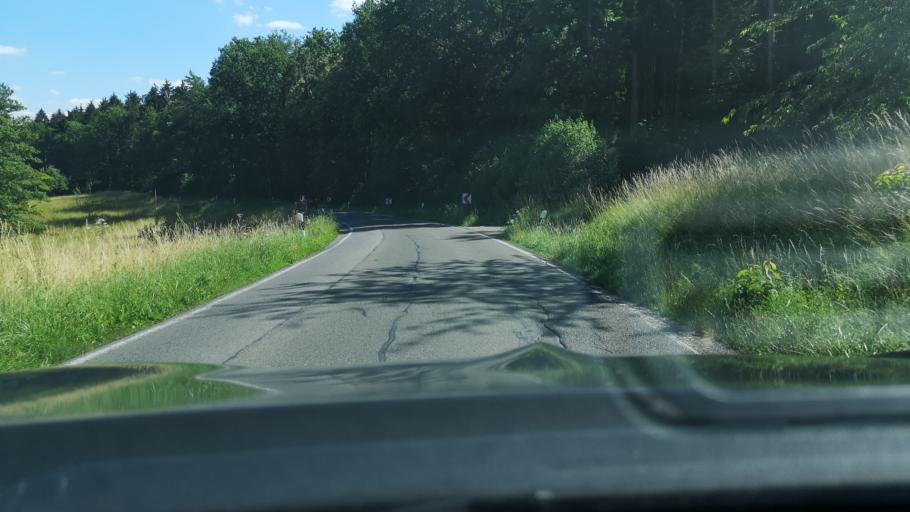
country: DE
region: Baden-Wuerttemberg
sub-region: Regierungsbezirk Stuttgart
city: Altenriet
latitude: 48.5849
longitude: 9.2184
